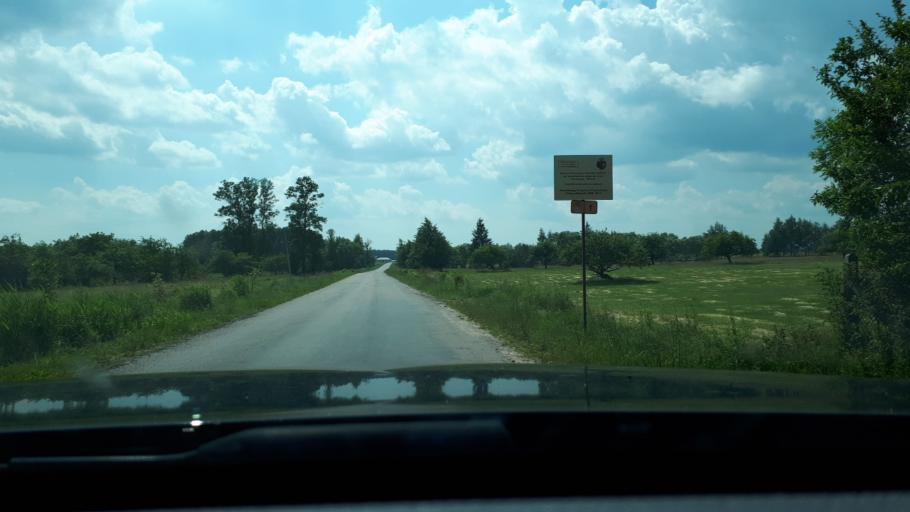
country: PL
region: Podlasie
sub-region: Powiat bialostocki
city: Choroszcz
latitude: 53.1123
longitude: 22.8855
